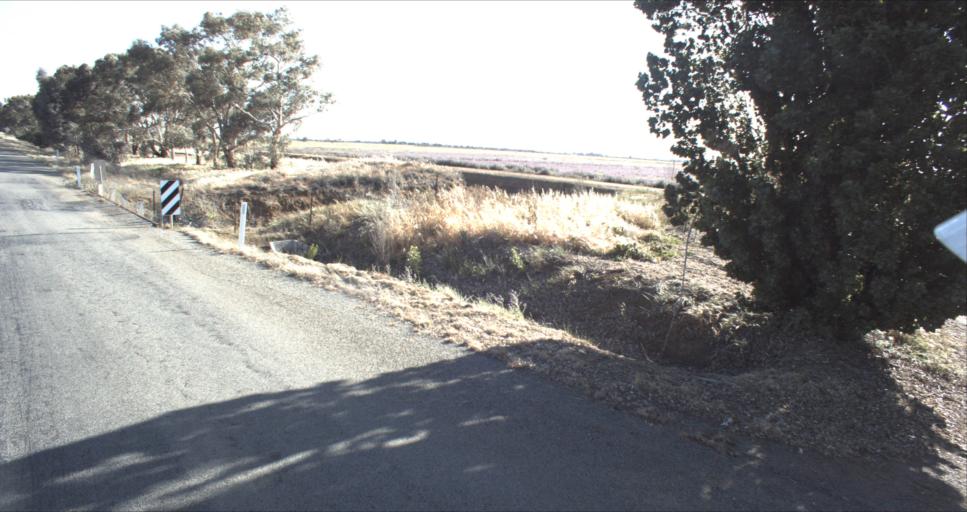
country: AU
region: New South Wales
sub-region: Leeton
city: Leeton
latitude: -34.5409
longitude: 146.2799
